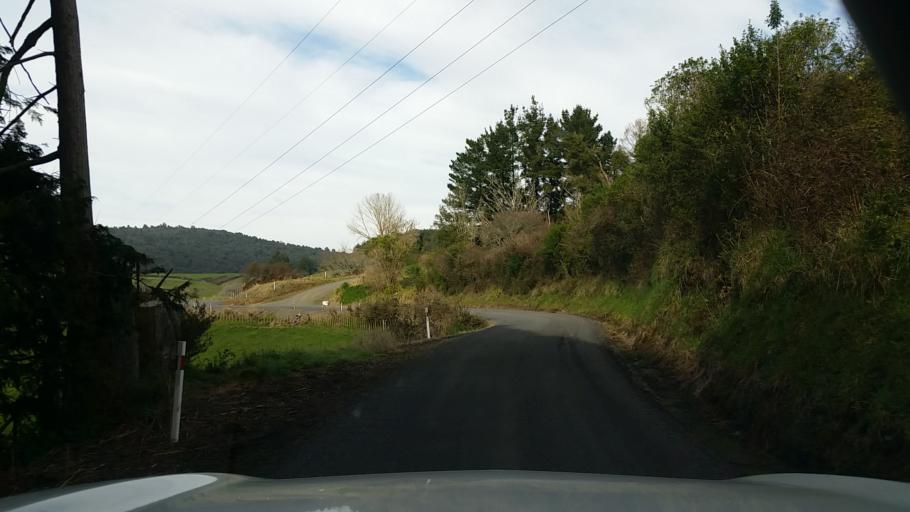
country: NZ
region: Waikato
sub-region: Matamata-Piako District
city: Matamata
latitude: -37.8063
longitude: 175.6354
